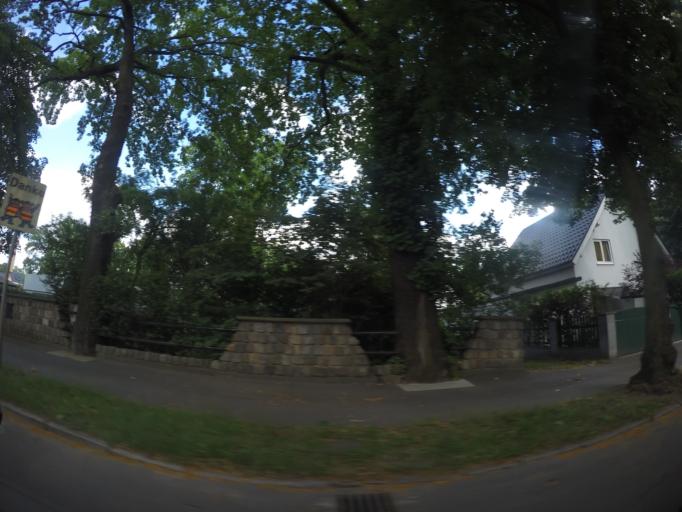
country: DE
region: Berlin
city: Biesdorf
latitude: 52.4903
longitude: 13.5608
